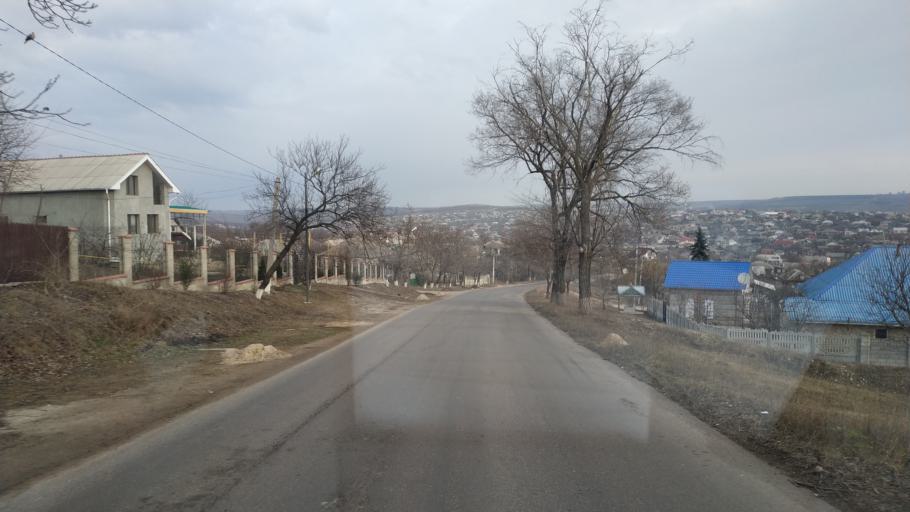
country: MD
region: Chisinau
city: Singera
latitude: 46.9539
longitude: 29.0577
